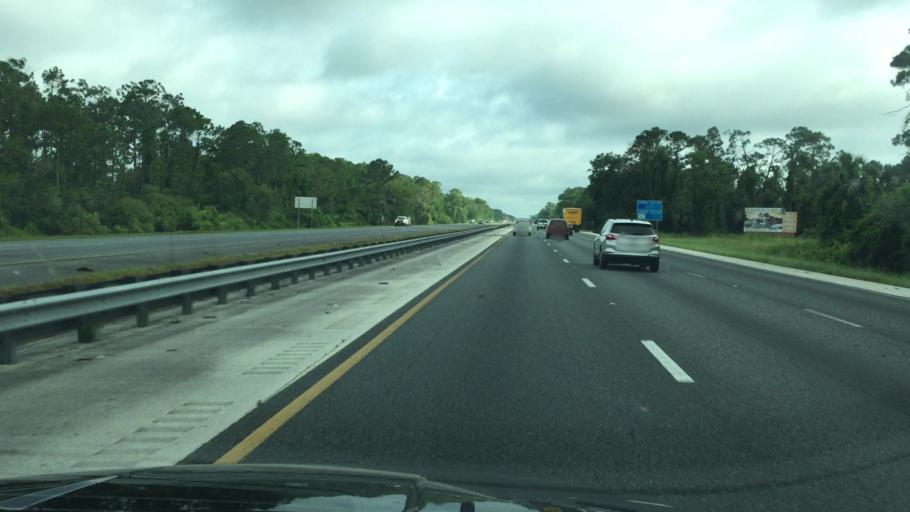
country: US
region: Florida
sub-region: Flagler County
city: Flagler Beach
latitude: 29.3876
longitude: -81.1481
